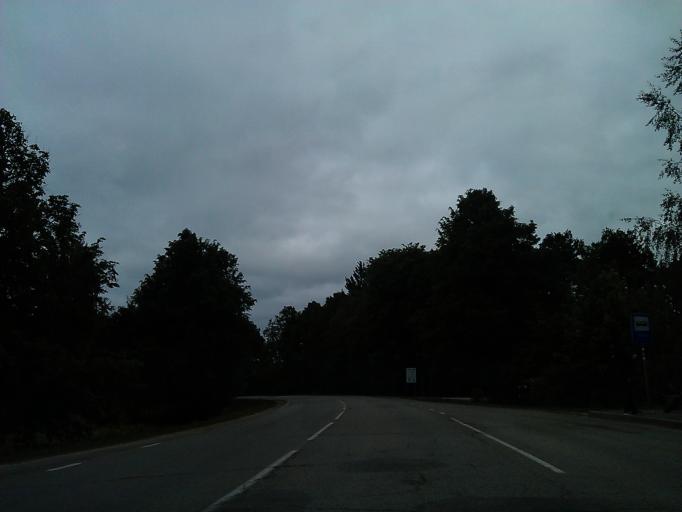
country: LV
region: Carnikava
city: Carnikava
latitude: 57.1253
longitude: 24.2962
